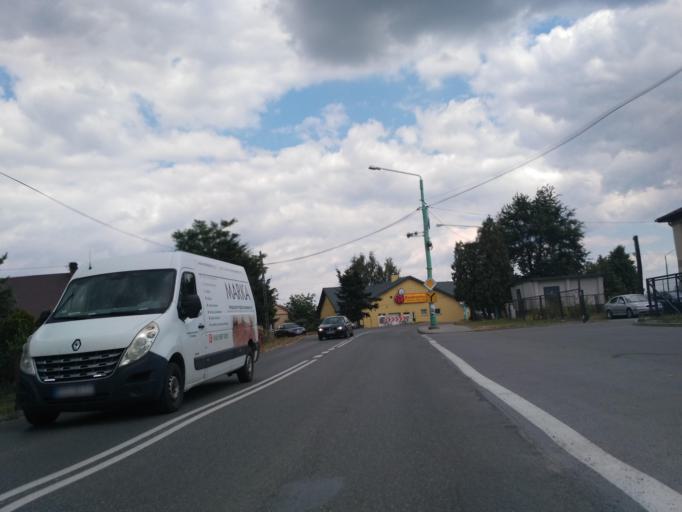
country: PL
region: Subcarpathian Voivodeship
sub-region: Powiat debicki
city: Zyrakow
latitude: 50.0631
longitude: 21.3591
